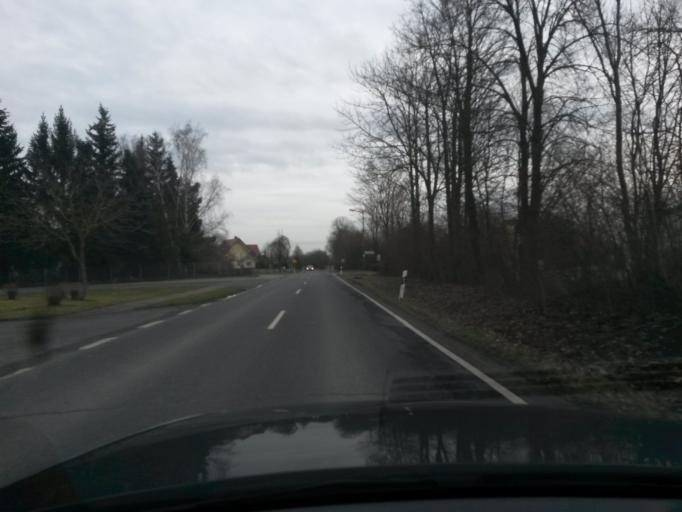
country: DE
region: Bavaria
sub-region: Regierungsbezirk Unterfranken
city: Bergtheim
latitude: 49.8953
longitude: 10.0690
